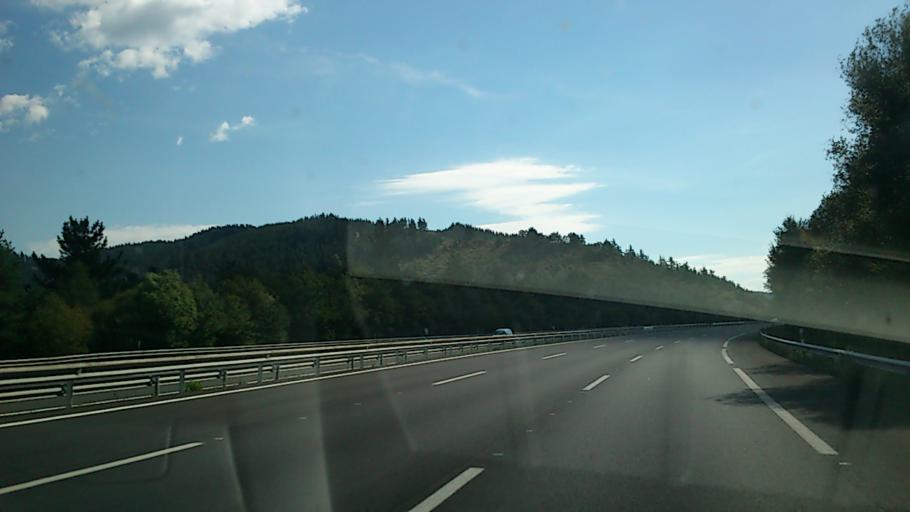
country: ES
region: Basque Country
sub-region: Provincia de Alava
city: Lezama
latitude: 43.0492
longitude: -2.9254
